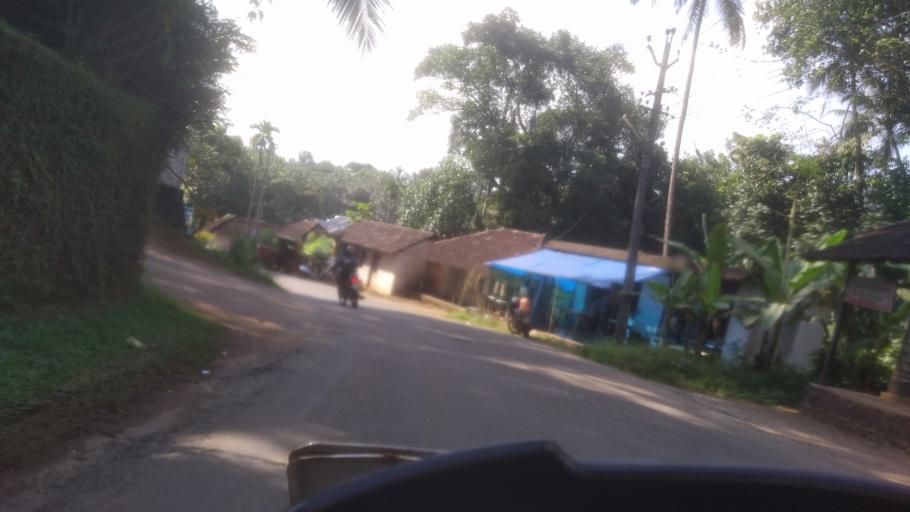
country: IN
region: Kerala
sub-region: Ernakulam
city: Kotamangalam
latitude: 10.0048
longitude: 76.6944
